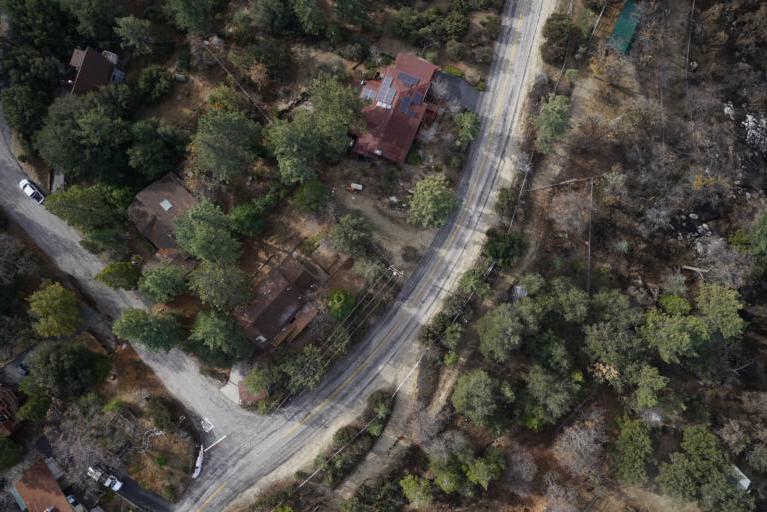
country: US
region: California
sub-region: Riverside County
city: Idyllwild
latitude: 33.7276
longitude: -116.7176
